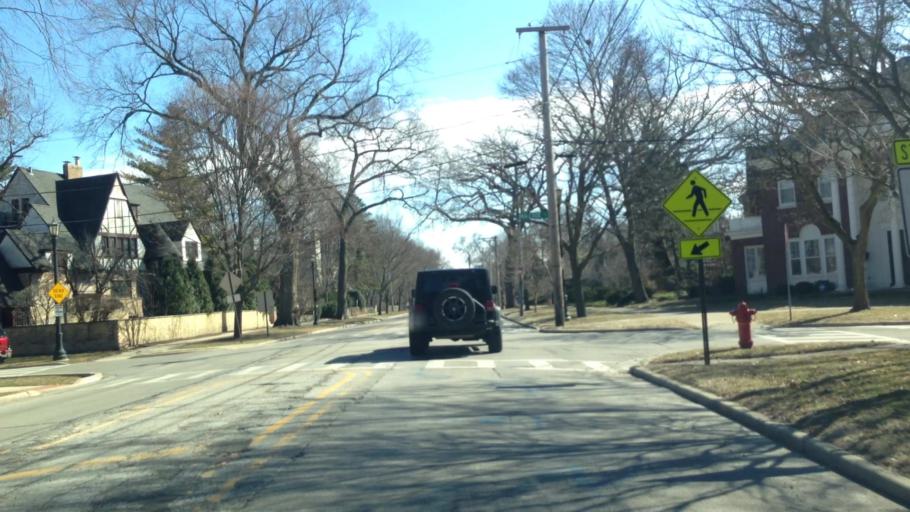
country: US
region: Illinois
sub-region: Cook County
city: Evanston
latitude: 42.0673
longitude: -87.6785
